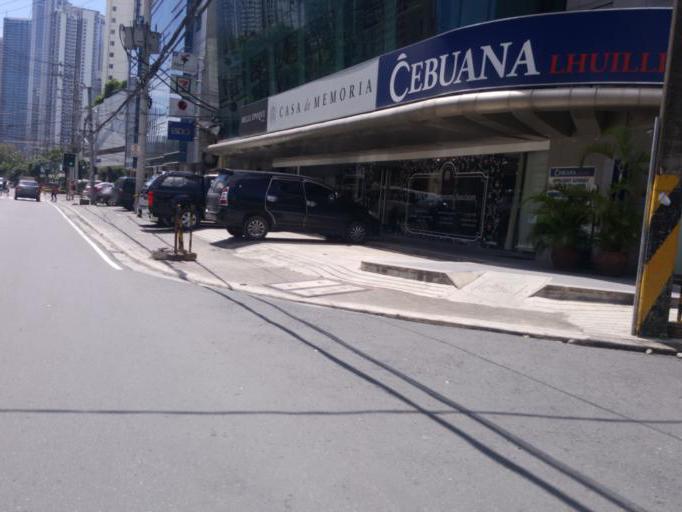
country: PH
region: Metro Manila
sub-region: Makati City
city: Makati City
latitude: 14.5629
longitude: 121.0231
